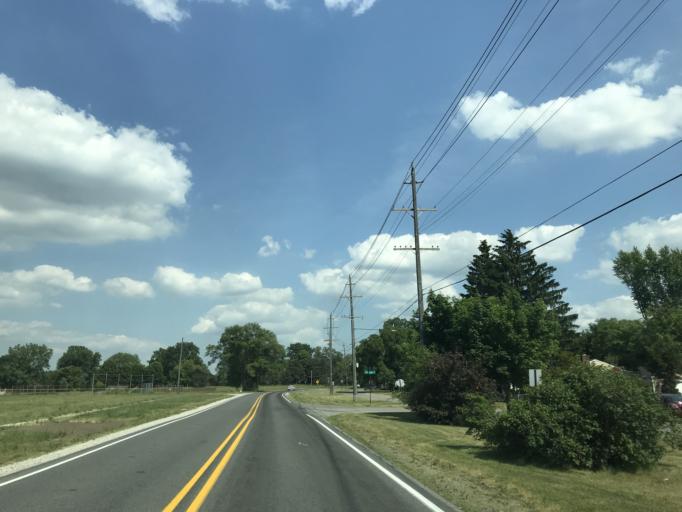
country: US
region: Michigan
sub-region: Washtenaw County
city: Ypsilanti
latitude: 42.2605
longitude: -83.5864
